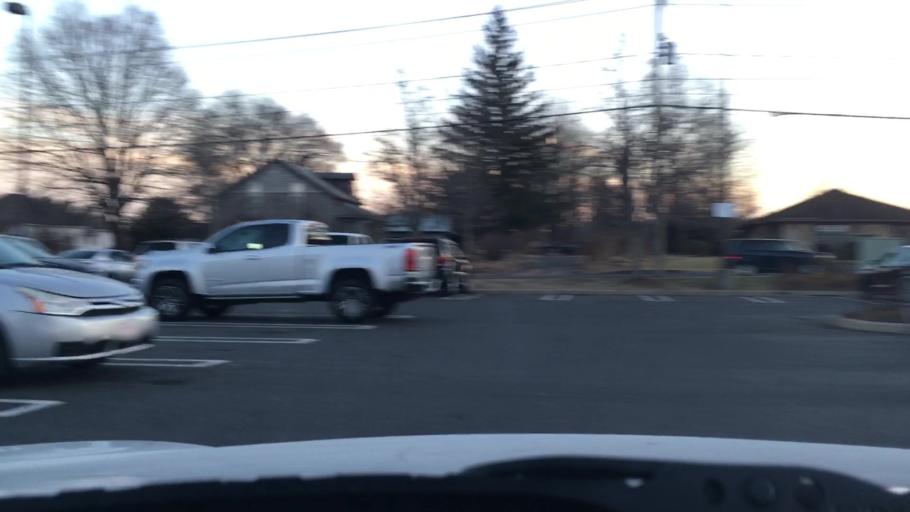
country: US
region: Massachusetts
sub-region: Hampden County
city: Agawam
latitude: 42.0679
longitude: -72.6743
